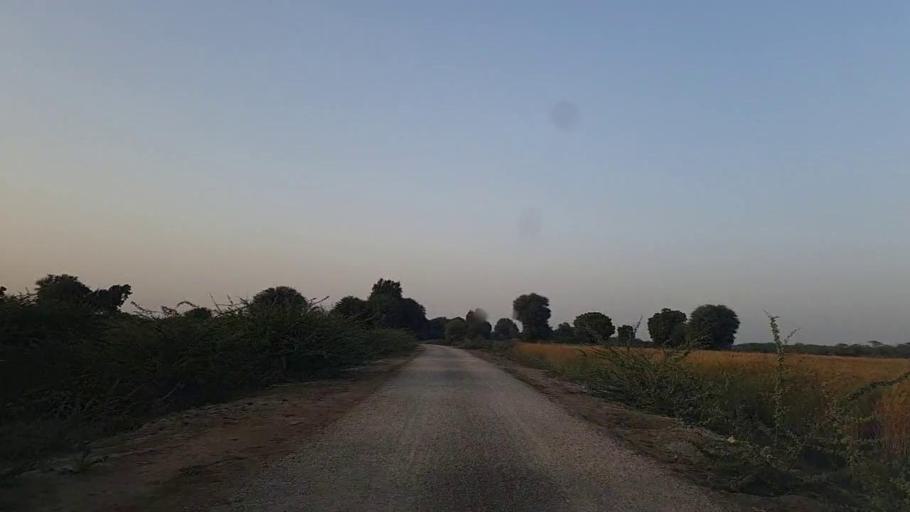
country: PK
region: Sindh
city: Naukot
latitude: 24.6986
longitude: 69.2733
